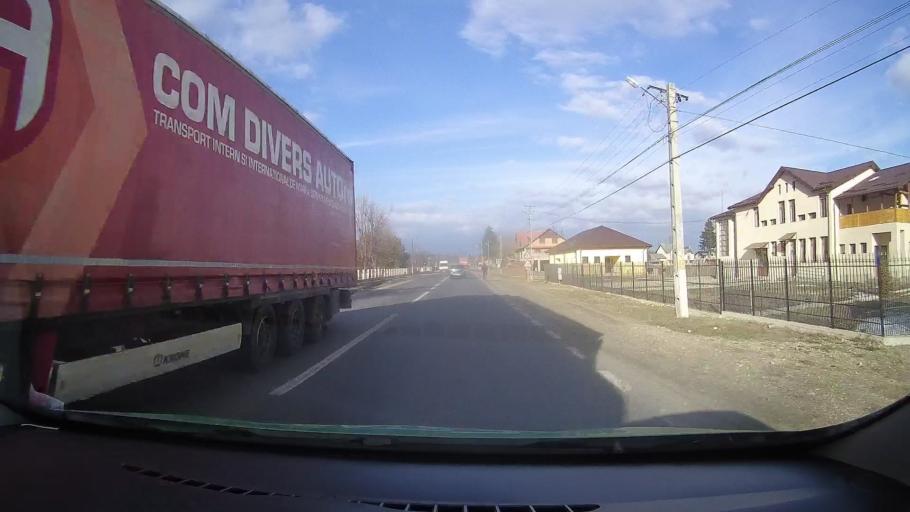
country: RO
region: Dambovita
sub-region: Comuna Ulmi
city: Viisoara
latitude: 44.8795
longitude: 25.4263
